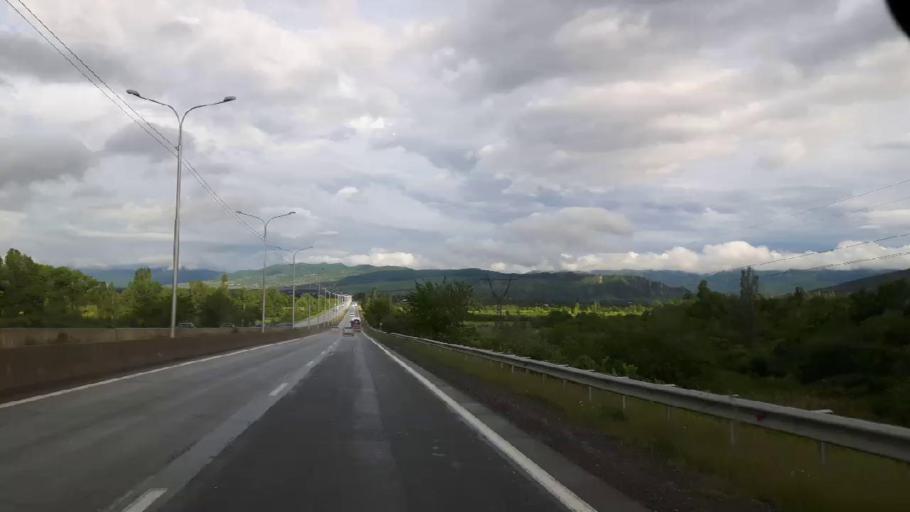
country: GE
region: Shida Kartli
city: Kaspi
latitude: 41.9260
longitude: 44.5365
